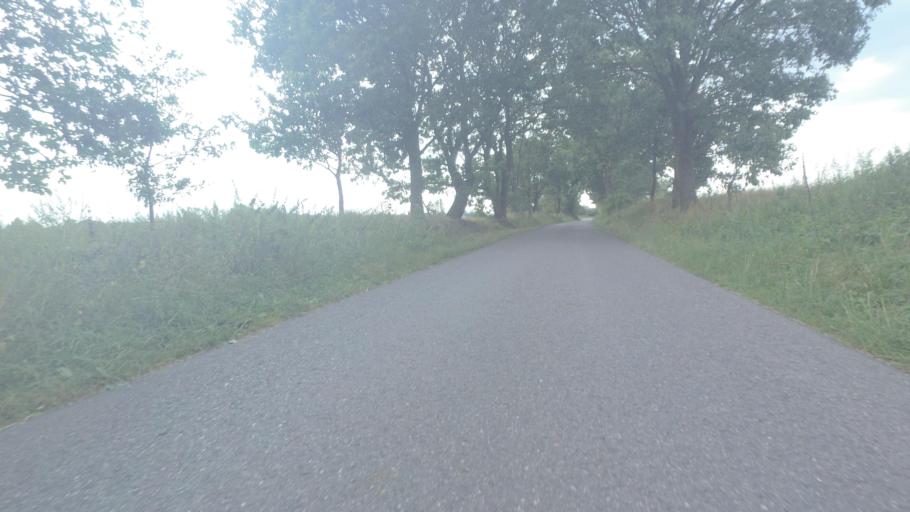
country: DE
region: Brandenburg
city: Wittstock
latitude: 53.2396
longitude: 12.4343
